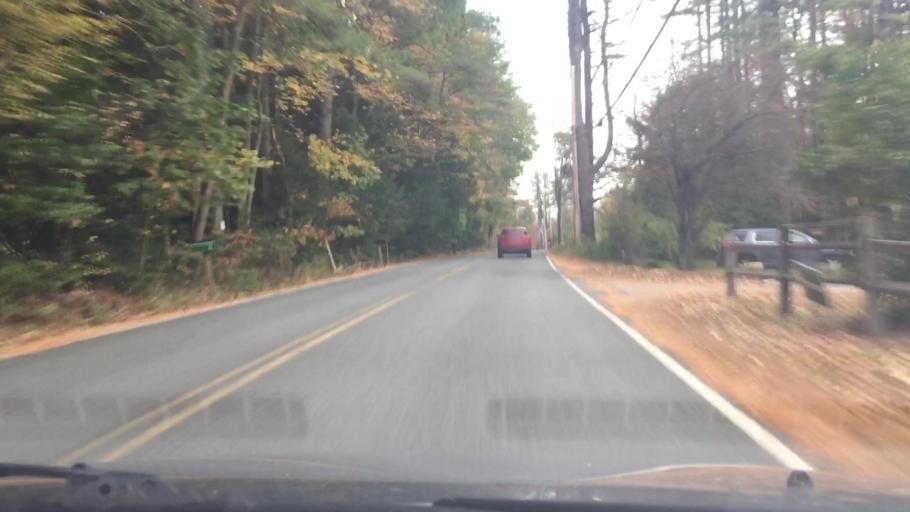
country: US
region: New Hampshire
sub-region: Cheshire County
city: Keene
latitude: 42.9046
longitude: -72.2880
